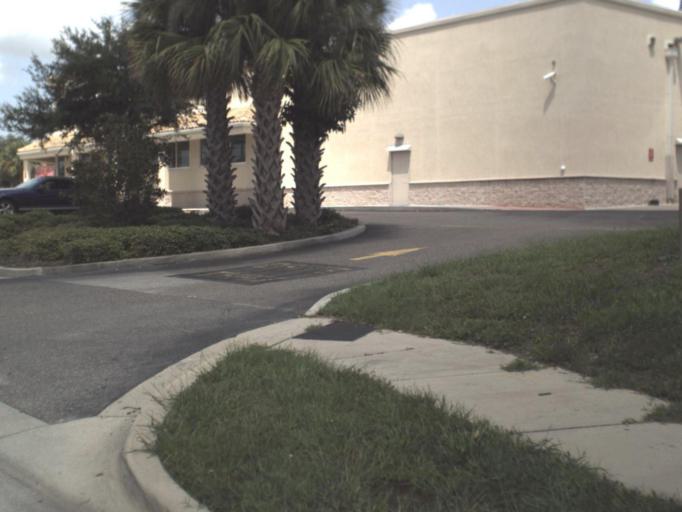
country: US
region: Florida
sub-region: Pinellas County
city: Safety Harbor
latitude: 27.9827
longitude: -82.7076
